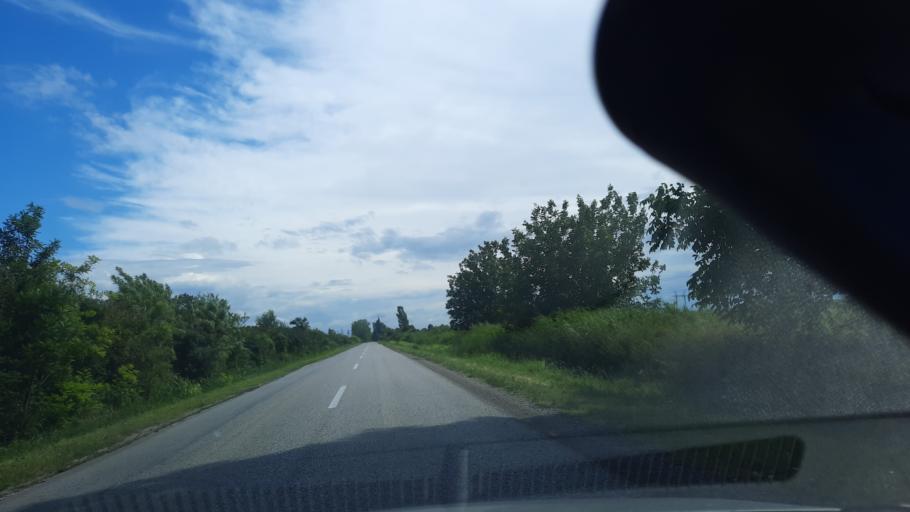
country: RS
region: Autonomna Pokrajina Vojvodina
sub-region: Sremski Okrug
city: Sremska Mitrovica
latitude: 45.0246
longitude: 19.6146
